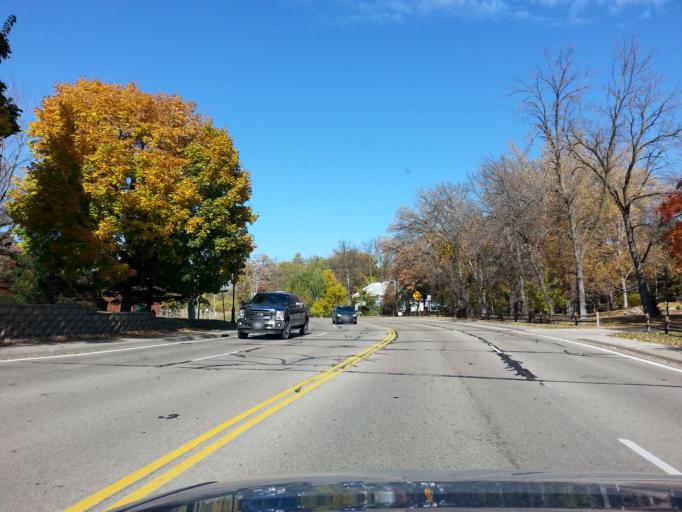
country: US
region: Minnesota
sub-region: Scott County
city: Prior Lake
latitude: 44.7201
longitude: -93.4377
